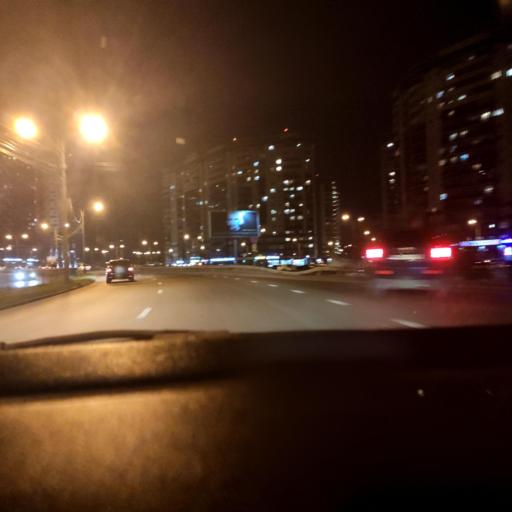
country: RU
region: Voronezj
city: Voronezh
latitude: 51.7124
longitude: 39.1948
